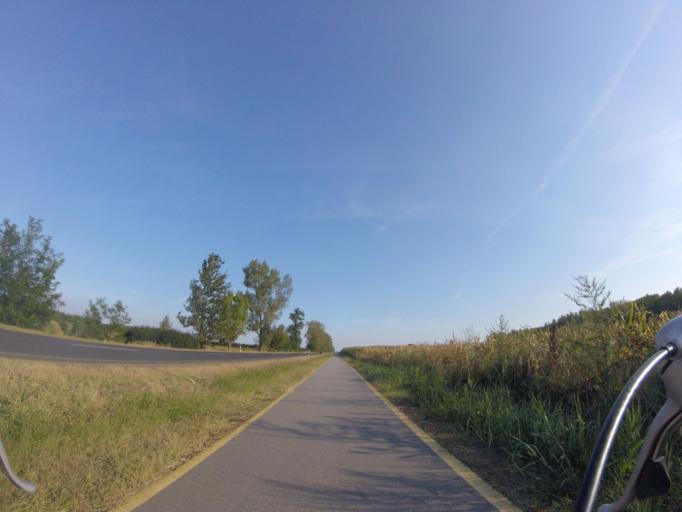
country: HU
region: Szabolcs-Szatmar-Bereg
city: Tiszanagyfalu
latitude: 48.1023
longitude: 21.4903
